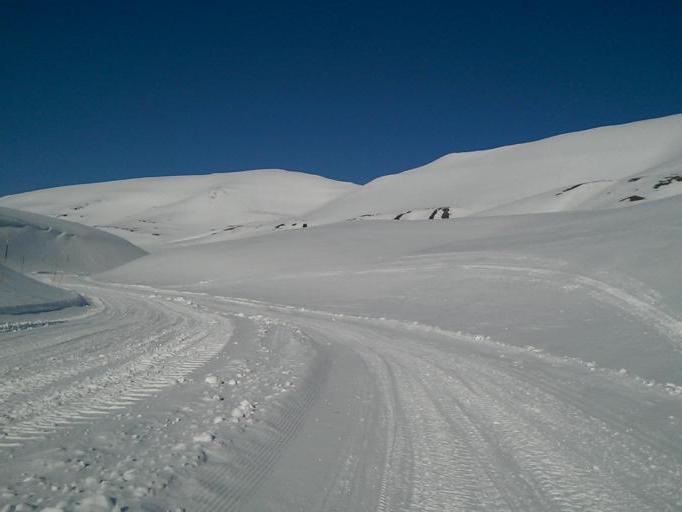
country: SJ
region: Svalbard
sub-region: Spitsbergen
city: Longyearbyen
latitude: 78.0476
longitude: 15.8761
